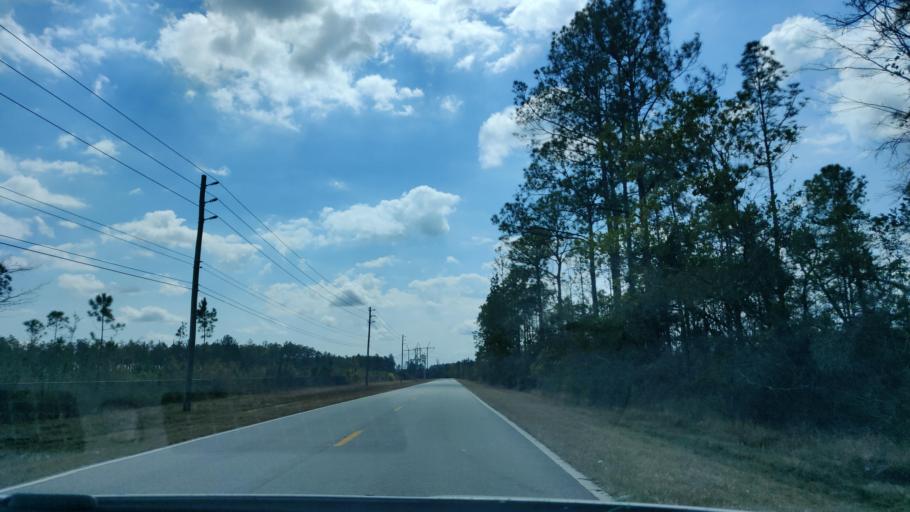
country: US
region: Florida
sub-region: Duval County
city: Baldwin
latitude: 30.2690
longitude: -81.9578
